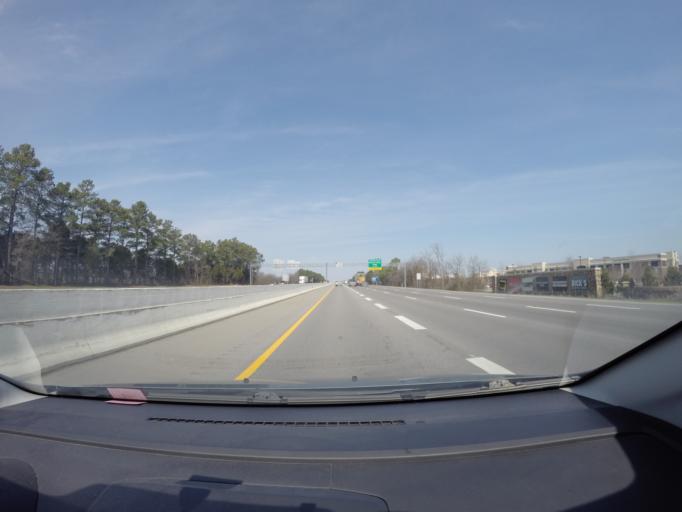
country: US
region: Tennessee
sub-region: Rutherford County
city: Murfreesboro
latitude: 35.8554
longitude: -86.4440
